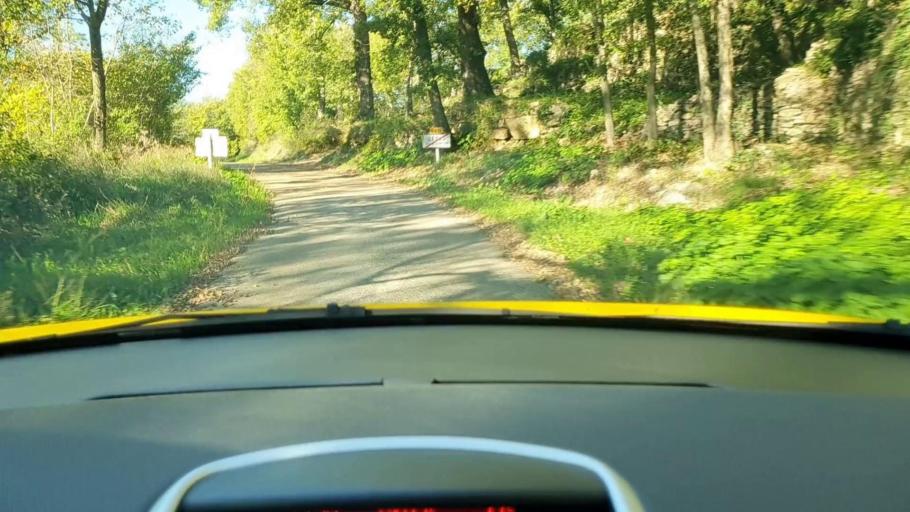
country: FR
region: Languedoc-Roussillon
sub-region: Departement du Gard
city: Sumene
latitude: 43.9758
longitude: 3.7776
